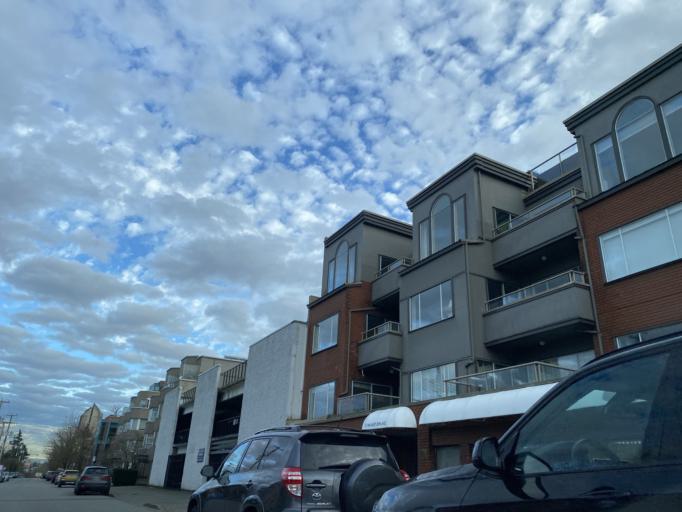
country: CA
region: British Columbia
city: Vancouver
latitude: 49.2644
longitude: -123.1311
